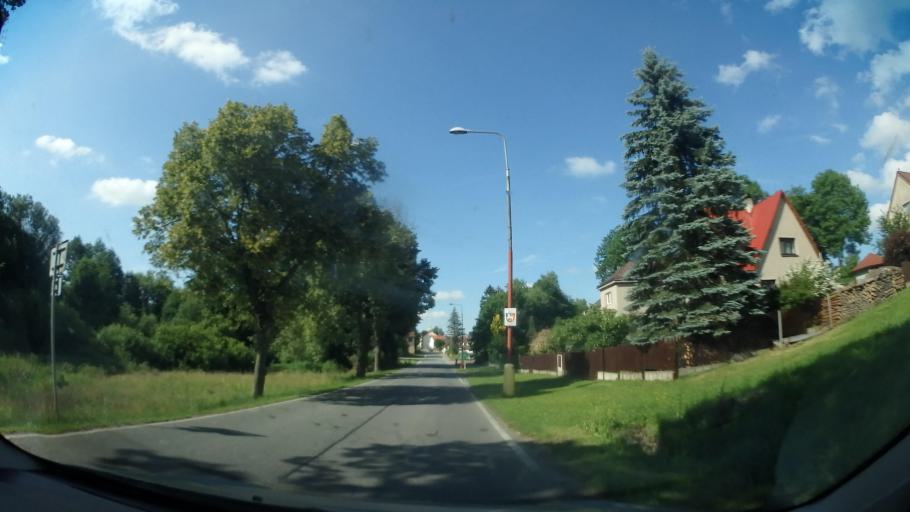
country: CZ
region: Vysocina
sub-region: Okres Zd'ar nad Sazavou
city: Svratka
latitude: 49.7175
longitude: 16.0342
